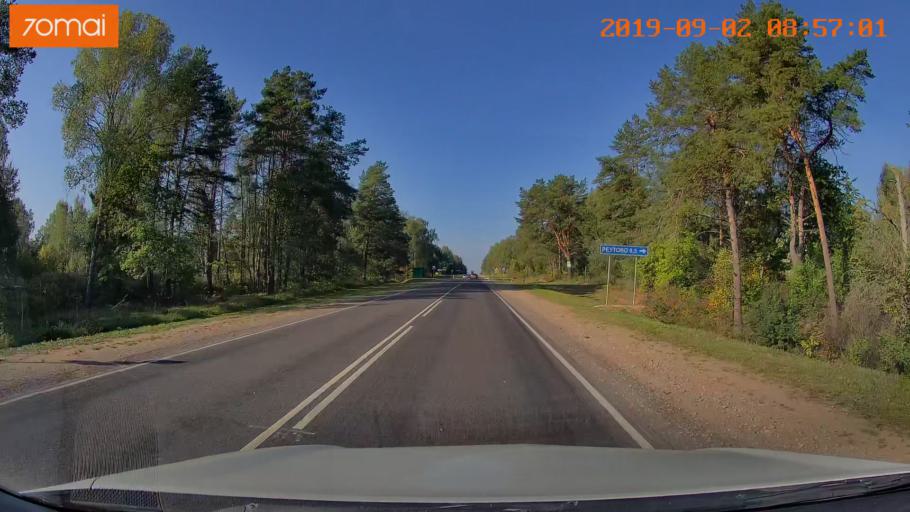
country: RU
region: Kaluga
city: Medyn'
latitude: 54.9404
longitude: 35.7784
